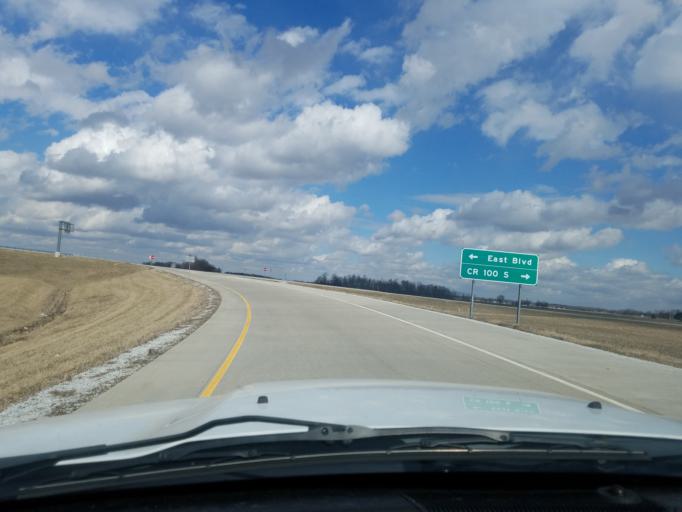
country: US
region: Indiana
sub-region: Howard County
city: Indian Heights
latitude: 40.4619
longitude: -86.0793
